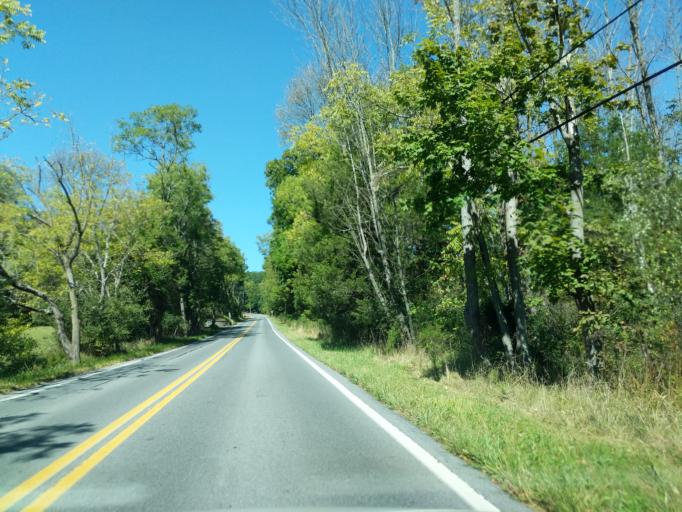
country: US
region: Pennsylvania
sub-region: Montgomery County
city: East Greenville
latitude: 40.4371
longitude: -75.4862
